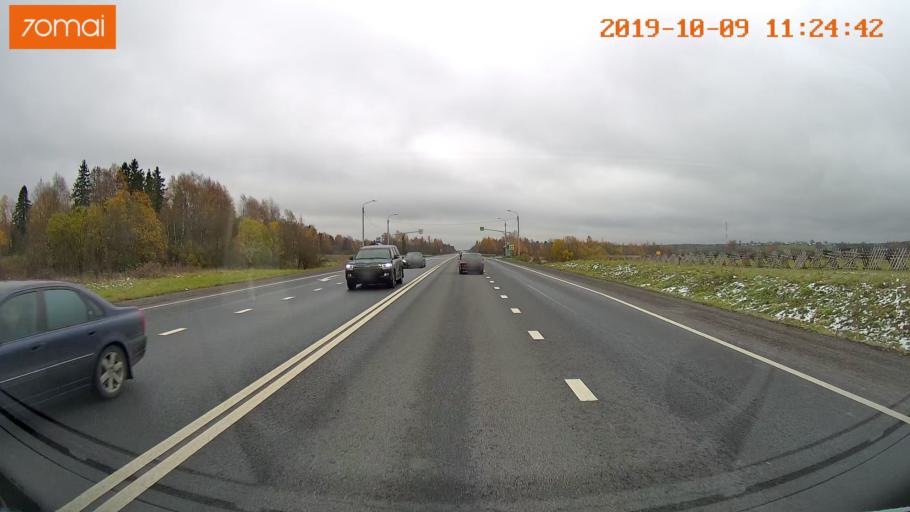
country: RU
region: Vologda
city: Vologda
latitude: 59.1090
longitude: 39.9827
